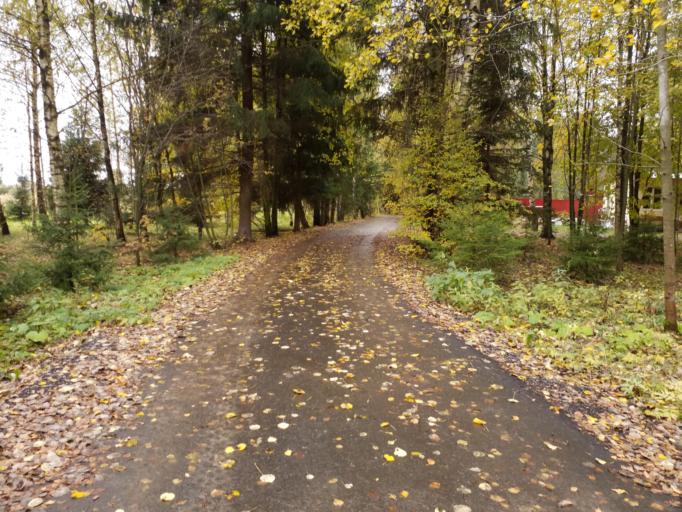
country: RU
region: Moskovskaya
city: Ashukino
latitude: 56.1601
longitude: 37.9599
